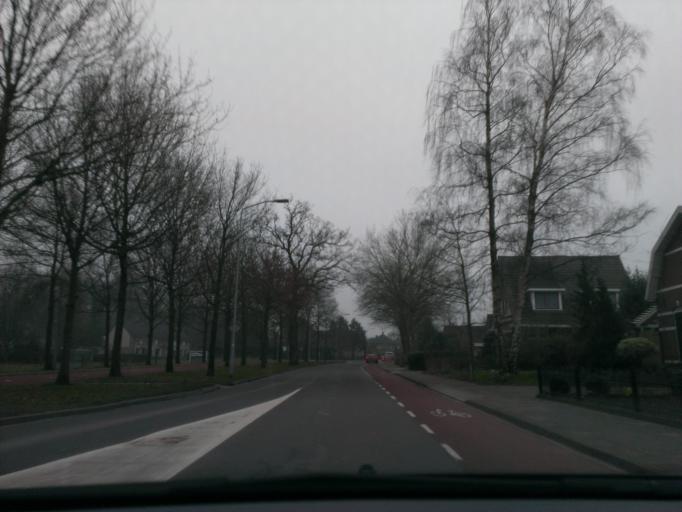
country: NL
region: Gelderland
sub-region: Gemeente Voorst
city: Twello
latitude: 52.2338
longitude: 6.1098
